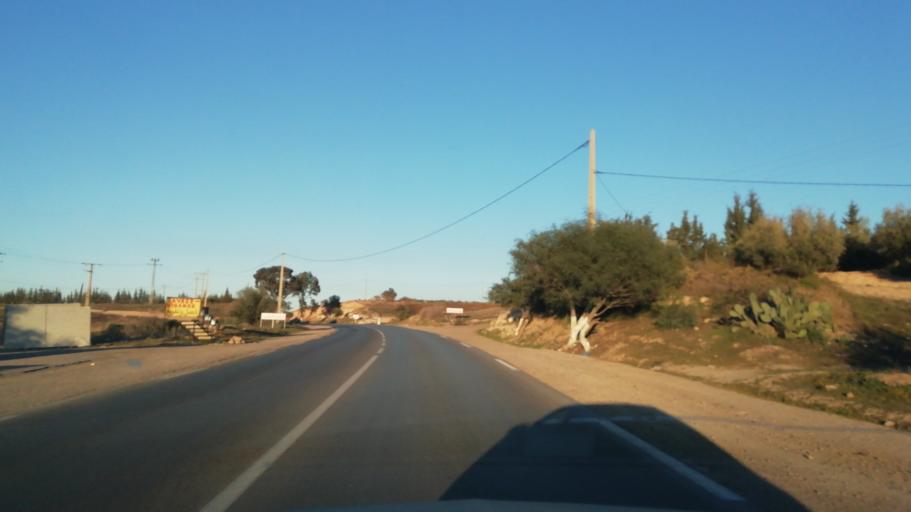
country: DZ
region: Tlemcen
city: Nedroma
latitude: 34.8553
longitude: -1.6804
